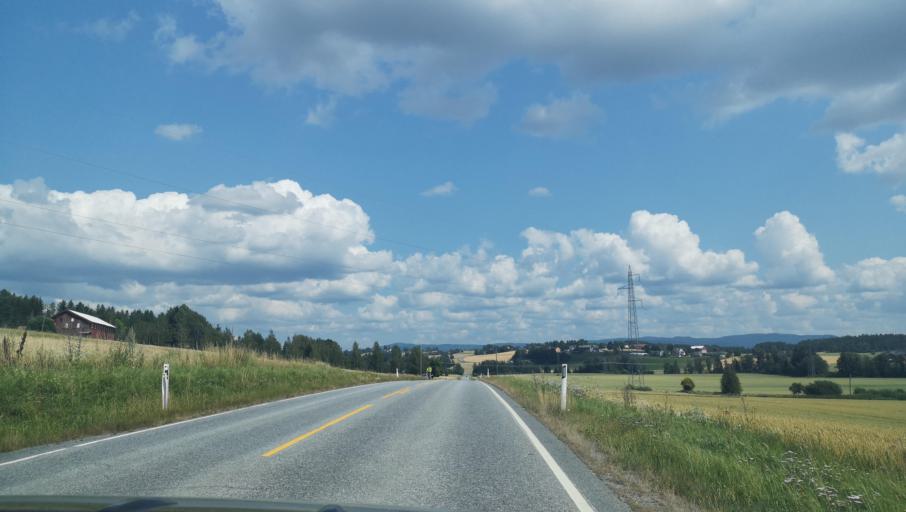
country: NO
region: Buskerud
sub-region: Ovre Eiker
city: Hokksund
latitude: 59.7174
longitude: 9.8229
